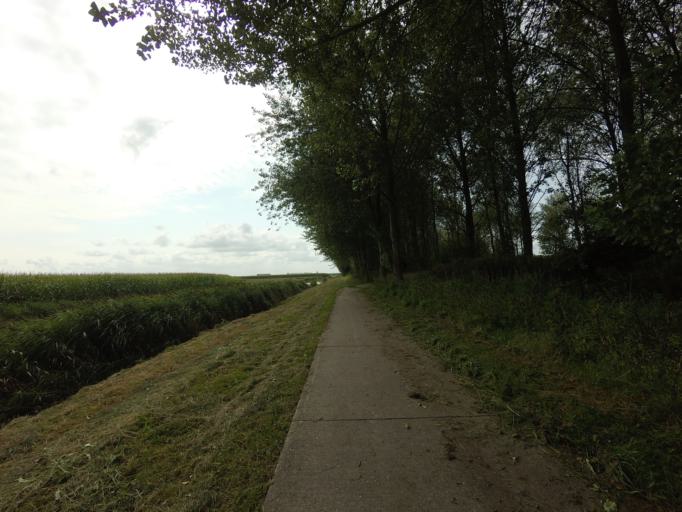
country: NL
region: North Holland
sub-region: Gemeente Edam-Volendam
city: Edam
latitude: 52.5041
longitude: 5.0070
